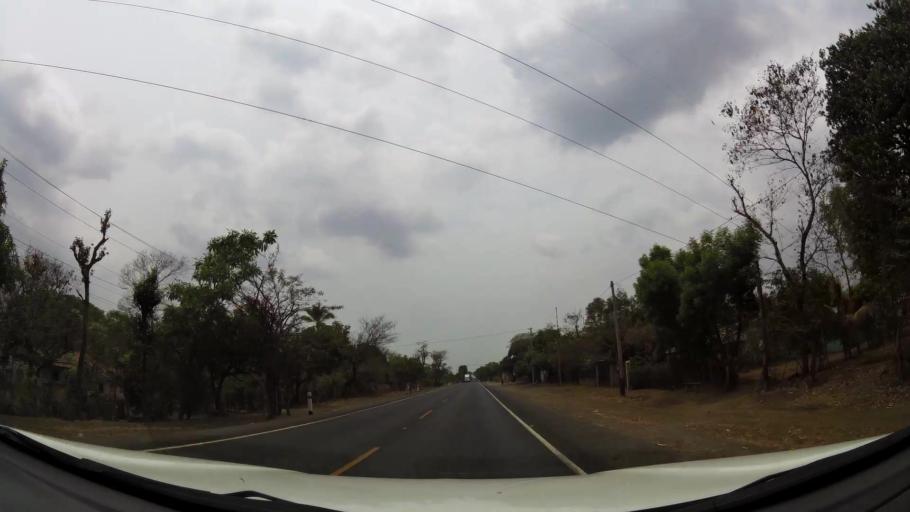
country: NI
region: Leon
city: Telica
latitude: 12.5271
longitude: -86.8814
